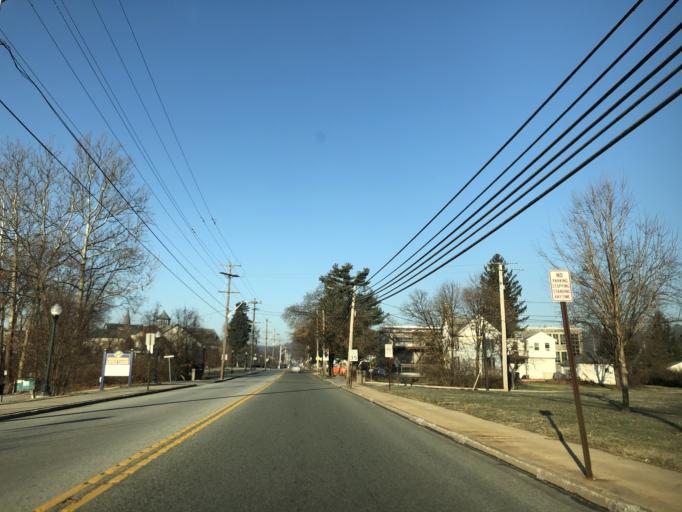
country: US
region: Pennsylvania
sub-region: Chester County
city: Downingtown
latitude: 40.0078
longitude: -75.7124
